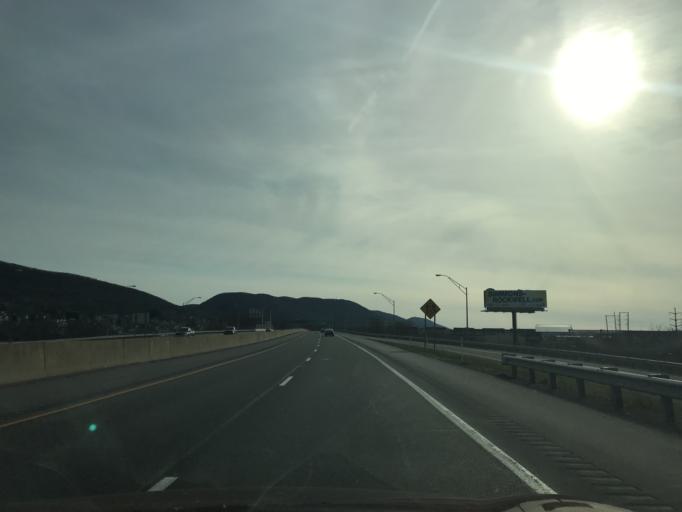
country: US
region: Pennsylvania
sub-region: Lycoming County
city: Williamsport
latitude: 41.2354
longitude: -77.0078
